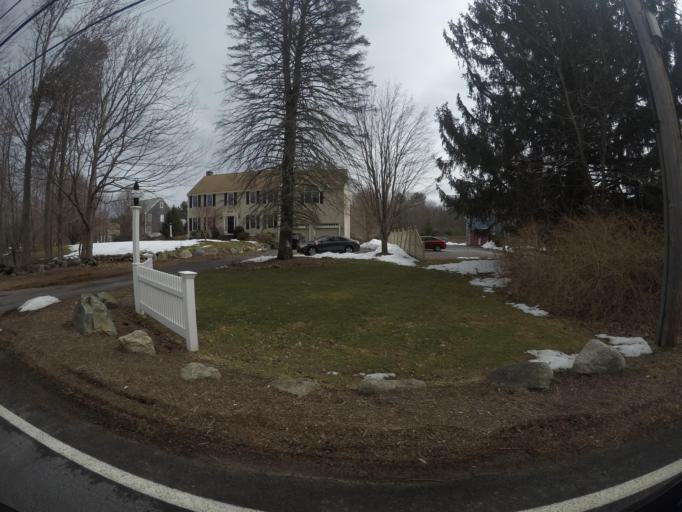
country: US
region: Massachusetts
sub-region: Bristol County
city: Easton
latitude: 42.0440
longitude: -71.1260
